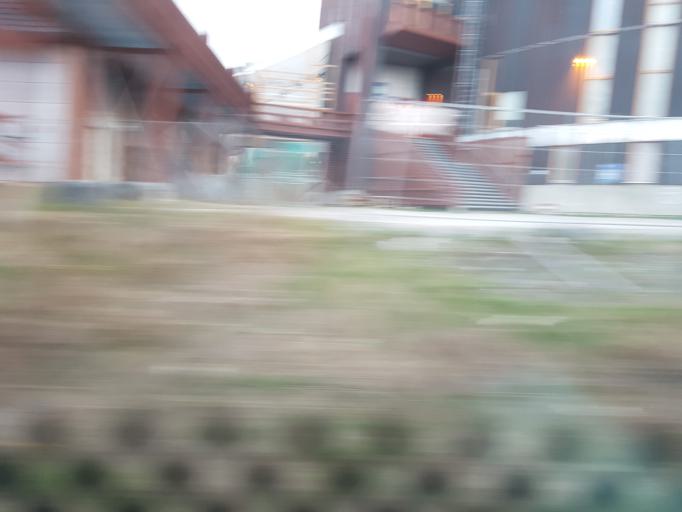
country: NO
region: Hedmark
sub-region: Hamar
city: Hamar
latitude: 60.8005
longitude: 11.0366
